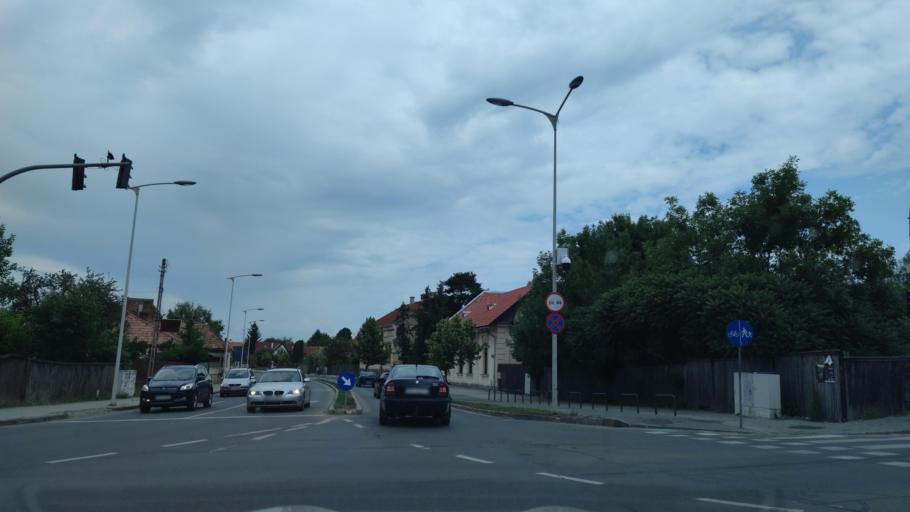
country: RO
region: Harghita
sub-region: Municipiul Miercurea Ciuc
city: Miercurea-Ciuc
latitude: 46.3683
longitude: 25.8059
